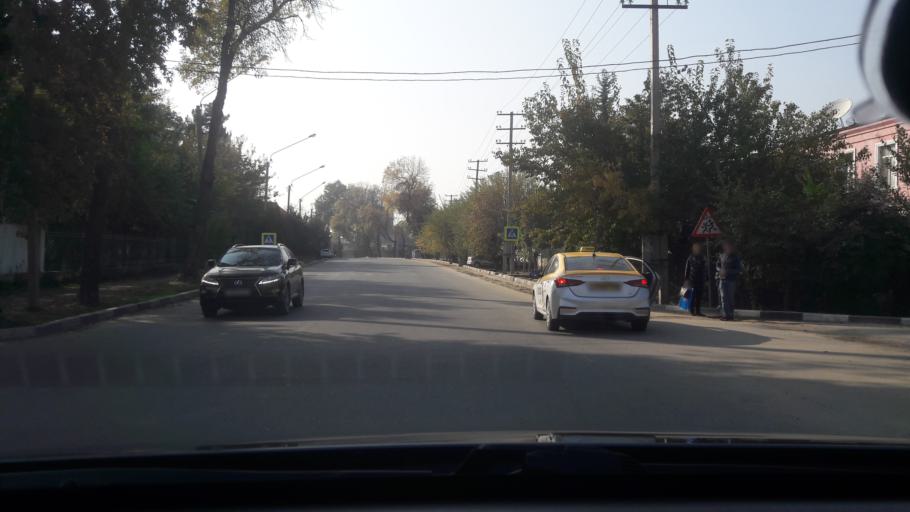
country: TJ
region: Dushanbe
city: Dushanbe
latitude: 38.5630
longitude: 68.7794
